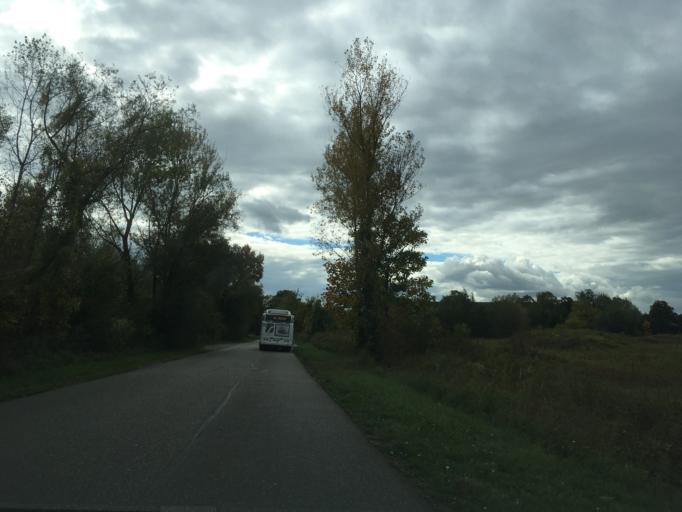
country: DE
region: Baden-Wuerttemberg
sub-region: Freiburg Region
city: Kehl
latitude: 48.5435
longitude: 7.7806
